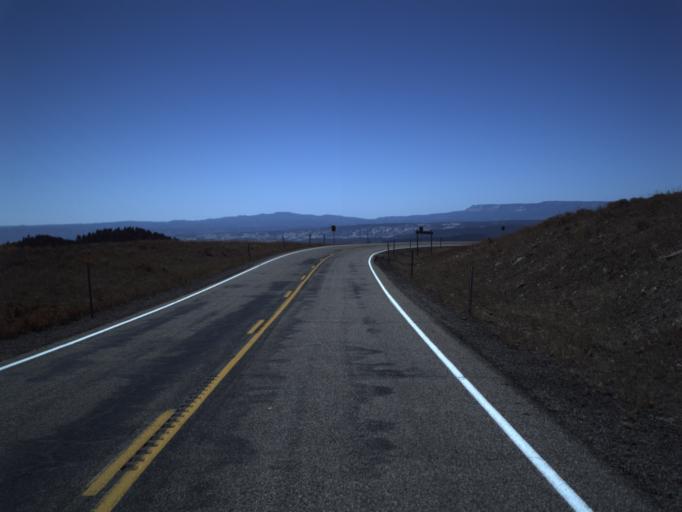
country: US
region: Utah
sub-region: Wayne County
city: Loa
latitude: 38.0109
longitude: -111.3761
